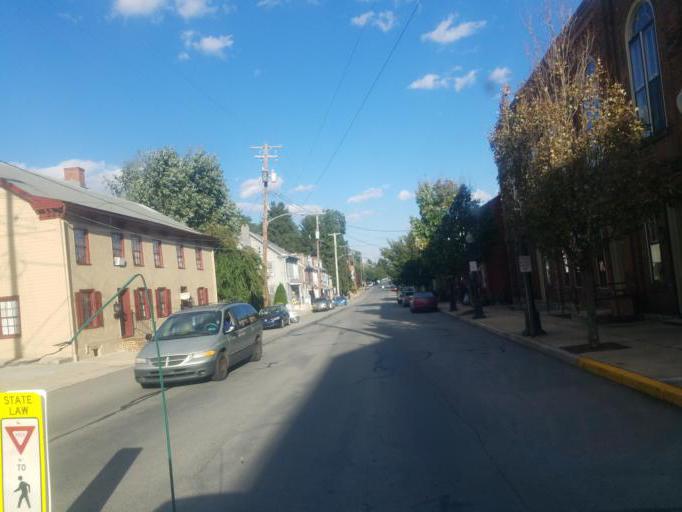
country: US
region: Pennsylvania
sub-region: Lancaster County
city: Marietta
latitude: 40.0573
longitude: -76.5522
